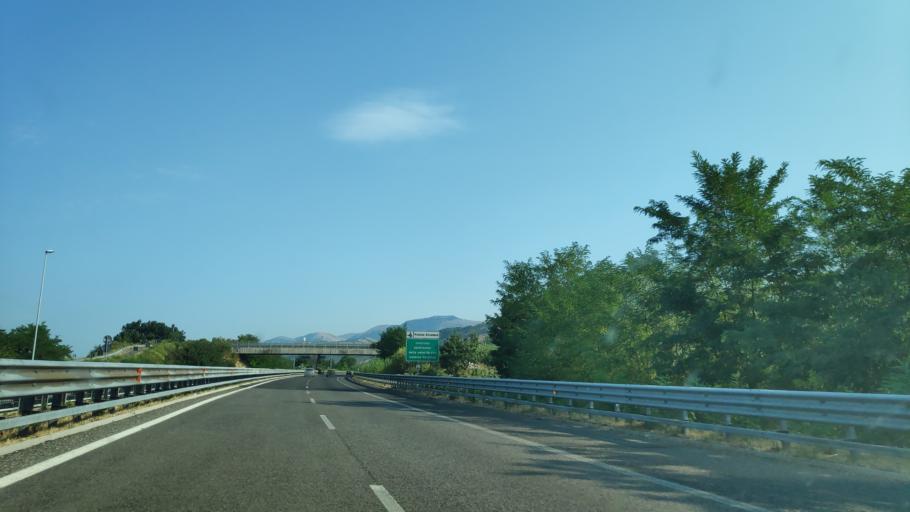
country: IT
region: Campania
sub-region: Provincia di Salerno
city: Atena Lucana
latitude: 40.4210
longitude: 15.5594
